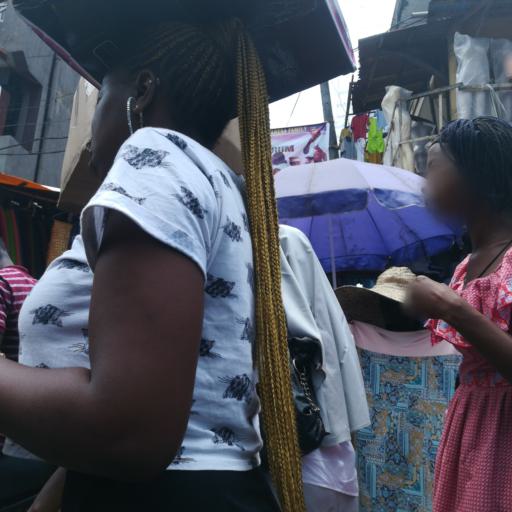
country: NG
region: Lagos
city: Lagos
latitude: 6.4612
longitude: 3.3870
